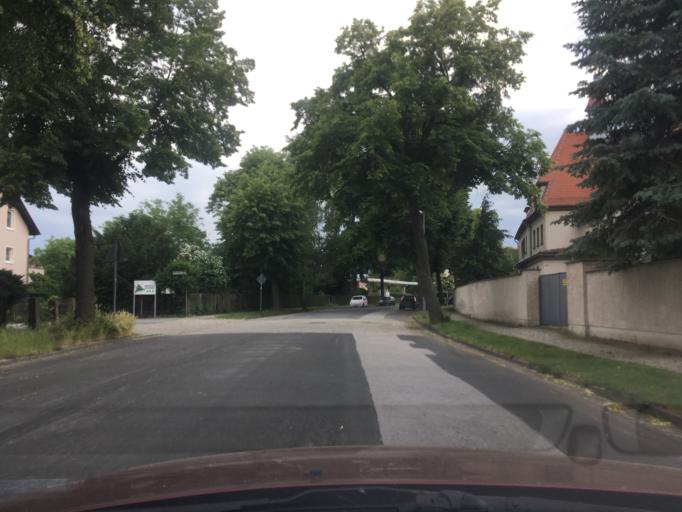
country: DE
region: Saxony
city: Bautzen
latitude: 51.1728
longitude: 14.4428
